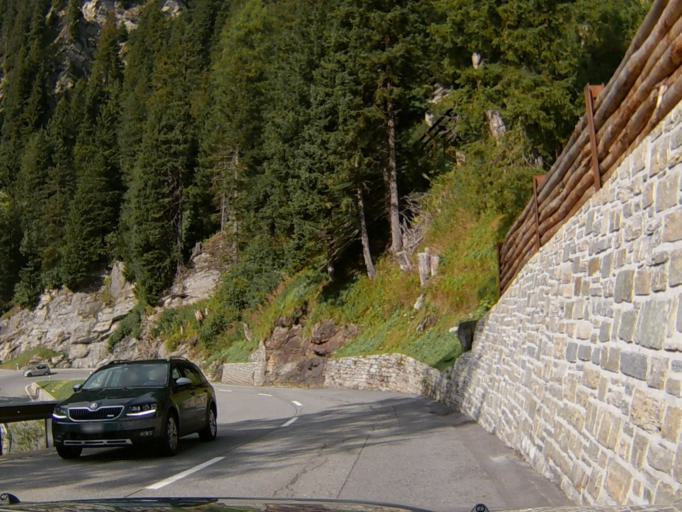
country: CH
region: Grisons
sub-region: Maloja District
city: Silvaplana
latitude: 46.3961
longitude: 9.6912
